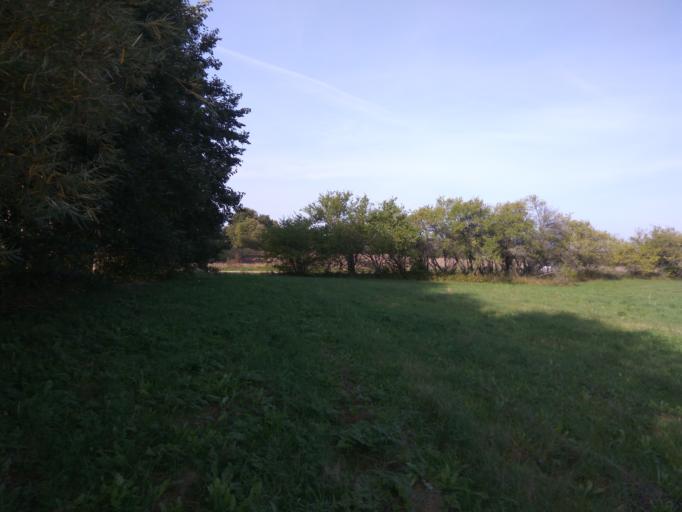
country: LV
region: Ventspils
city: Ventspils
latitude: 57.3547
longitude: 21.6401
